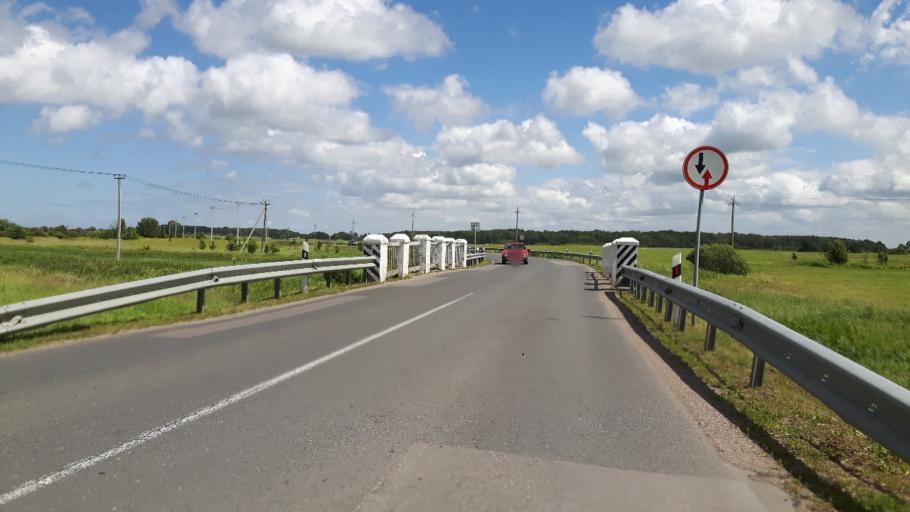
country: RU
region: Kaliningrad
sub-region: Zelenogradskiy Rayon
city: Zelenogradsk
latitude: 54.9289
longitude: 20.4209
